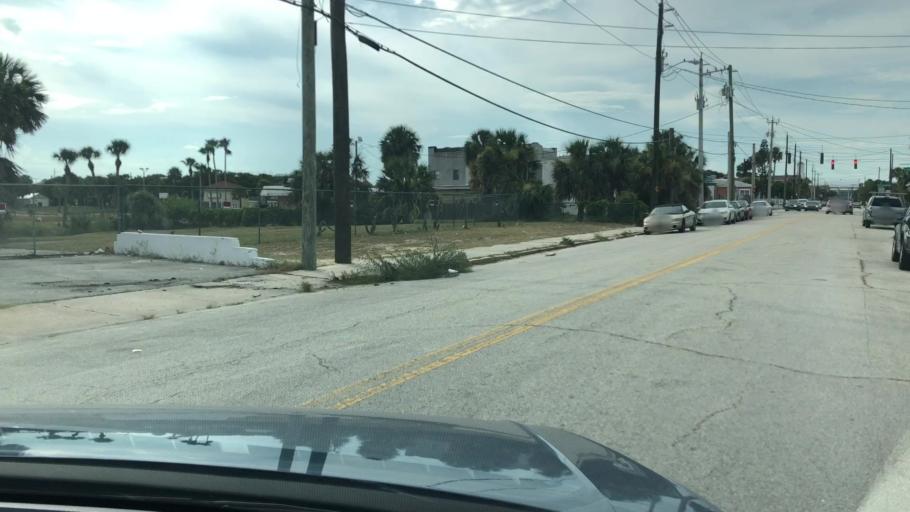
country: US
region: Florida
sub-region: Volusia County
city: Daytona Beach
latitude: 29.2205
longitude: -81.0067
